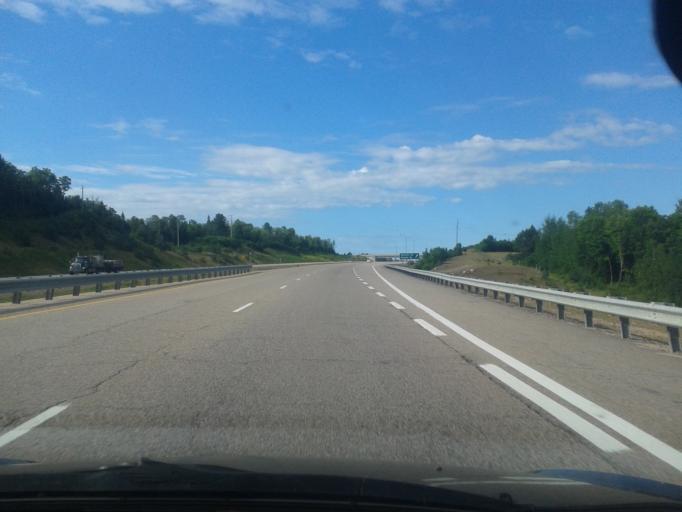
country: CA
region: Ontario
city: South River
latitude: 45.9075
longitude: -79.3669
